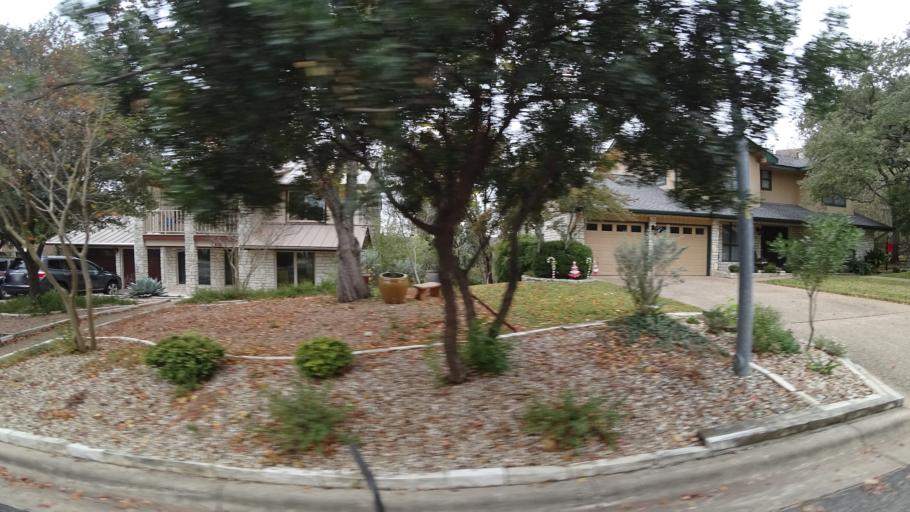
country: US
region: Texas
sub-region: Williamson County
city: Jollyville
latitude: 30.3723
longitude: -97.7953
